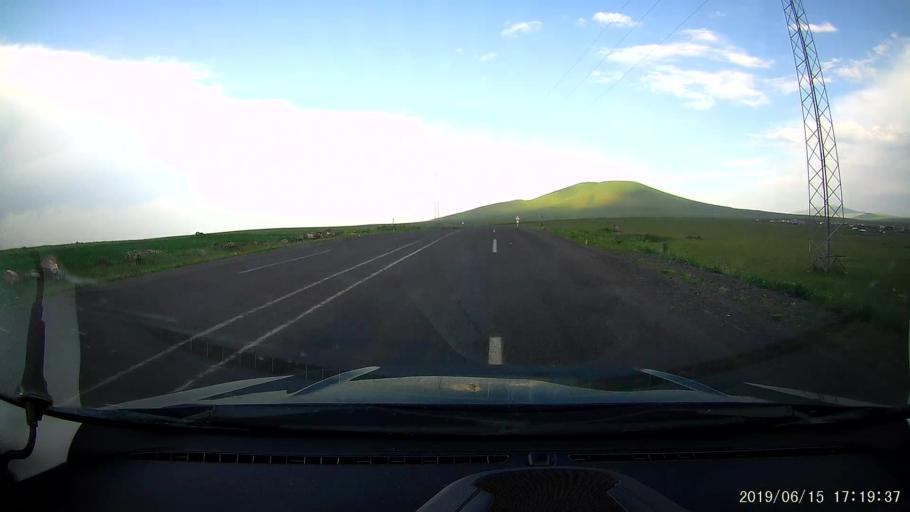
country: TR
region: Kars
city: Kars
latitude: 40.6164
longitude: 43.2822
